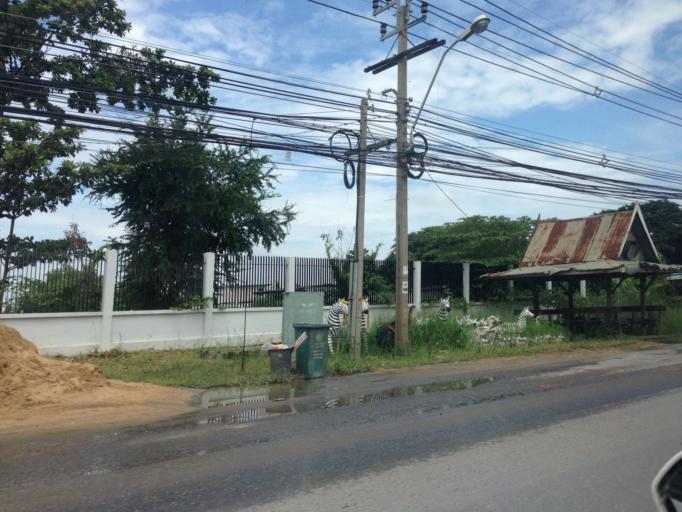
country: TH
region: Nonthaburi
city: Pak Kret
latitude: 13.9323
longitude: 100.5333
